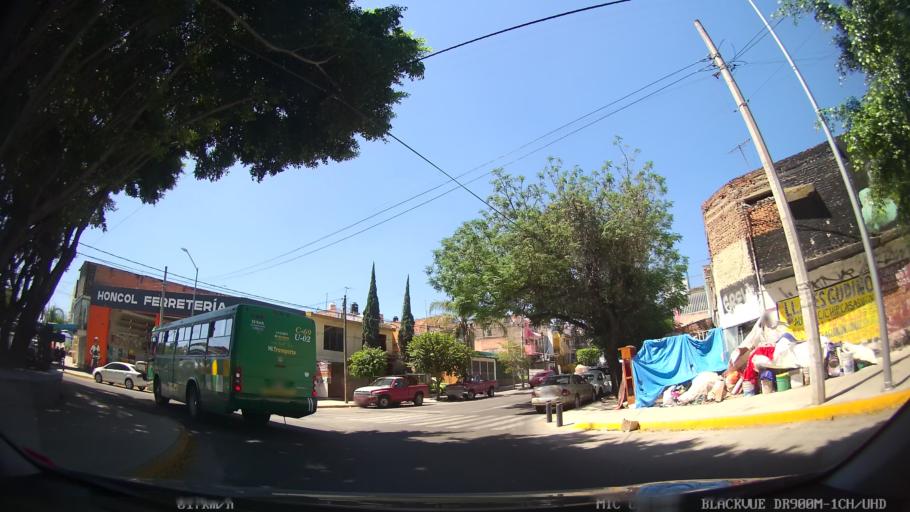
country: MX
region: Jalisco
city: Tlaquepaque
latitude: 20.6934
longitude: -103.2921
